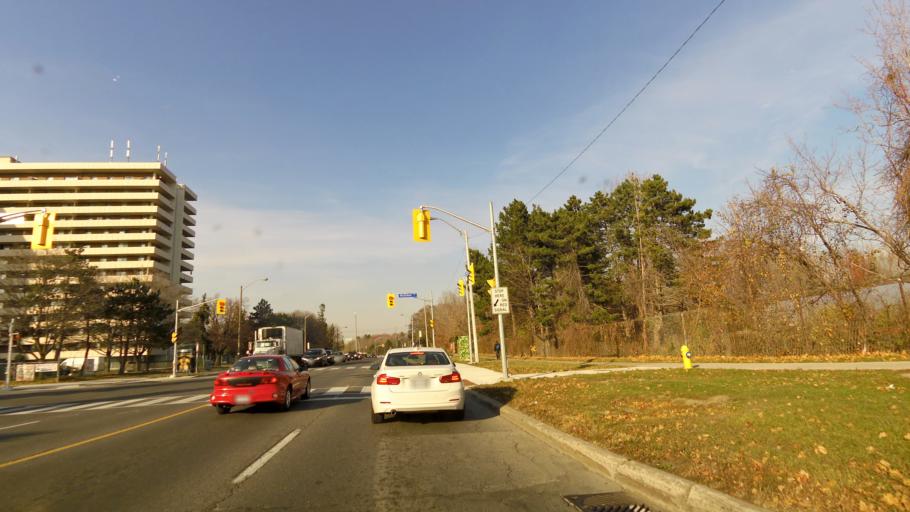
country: CA
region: Ontario
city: Concord
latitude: 43.7729
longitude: -79.5212
